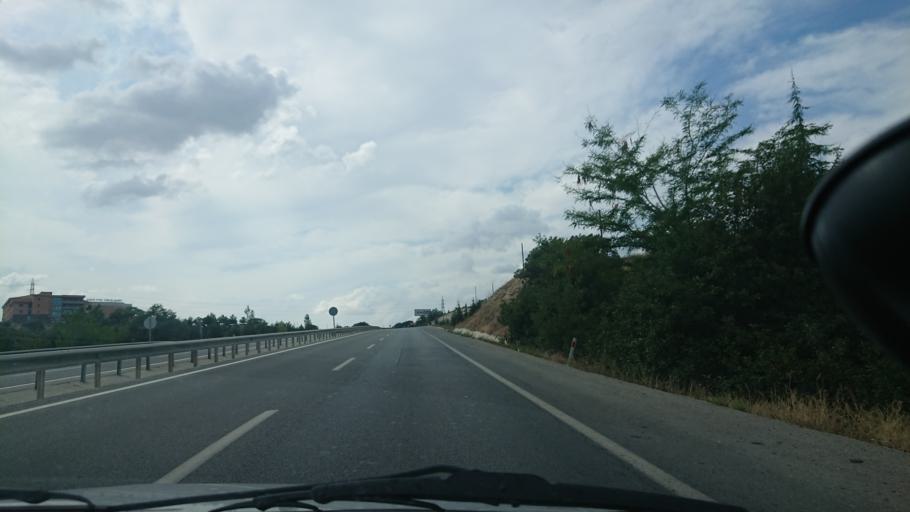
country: TR
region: Eskisehir
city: Eskisehir
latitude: 39.7423
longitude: 30.4007
